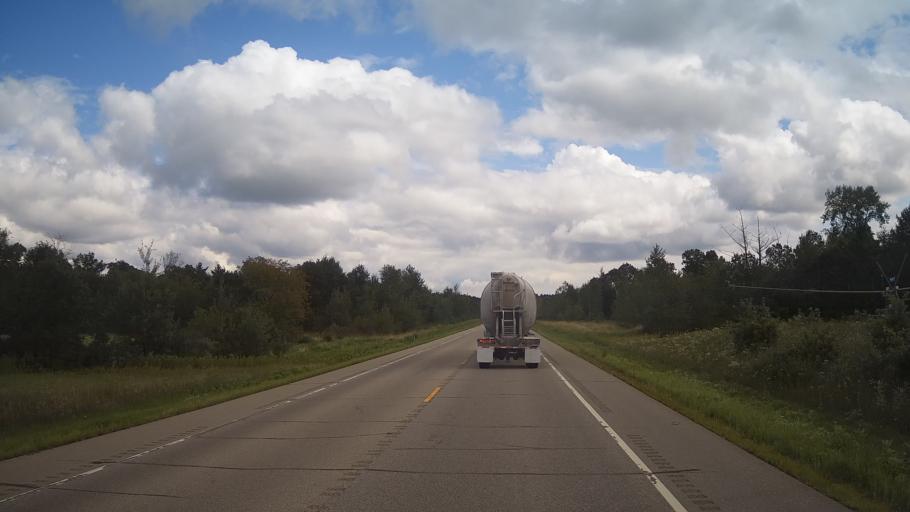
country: US
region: Wisconsin
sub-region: Adams County
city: Friendship
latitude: 44.0220
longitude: -89.6319
